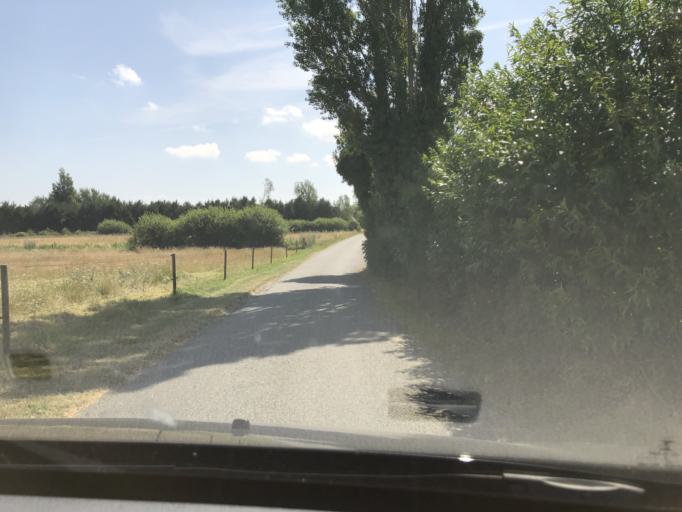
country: DK
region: South Denmark
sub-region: AEro Kommune
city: AEroskobing
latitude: 54.9281
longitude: 10.2884
